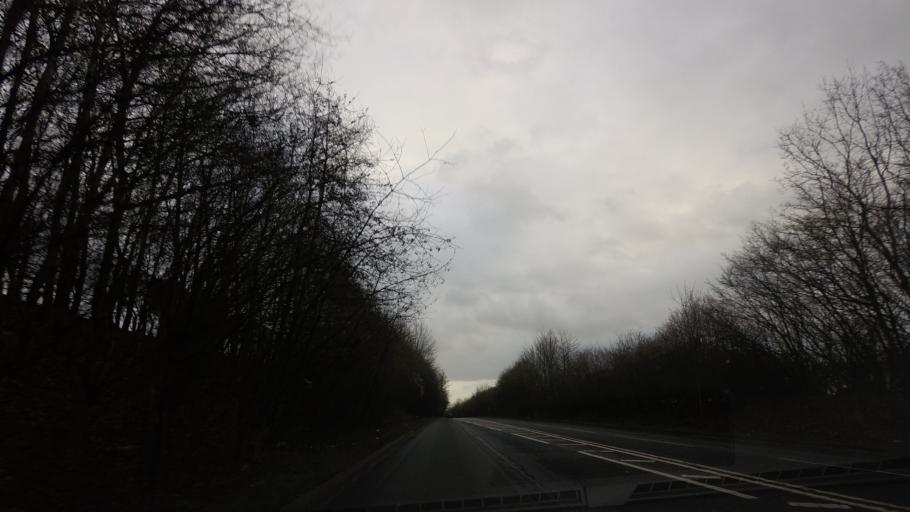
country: GB
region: England
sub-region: Kent
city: East Peckham
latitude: 51.2448
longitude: 0.3756
